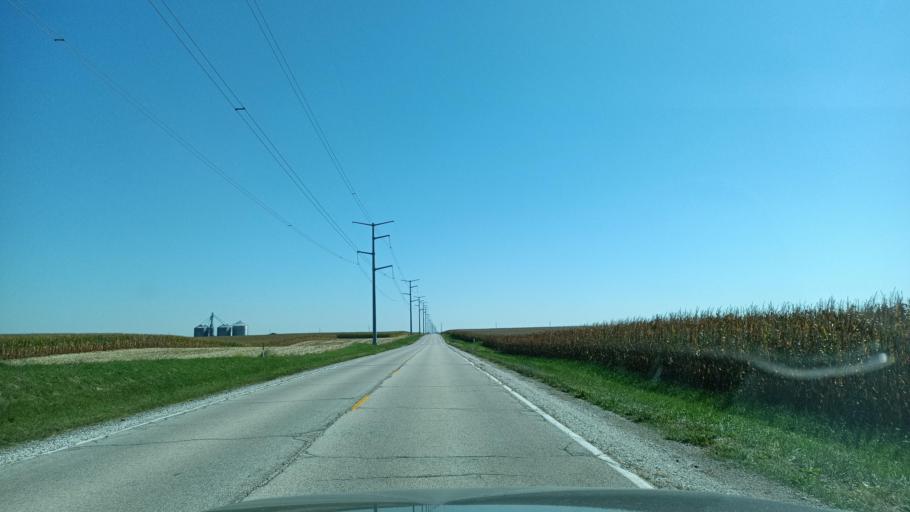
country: US
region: Illinois
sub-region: Peoria County
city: Elmwood
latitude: 40.9024
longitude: -90.0279
